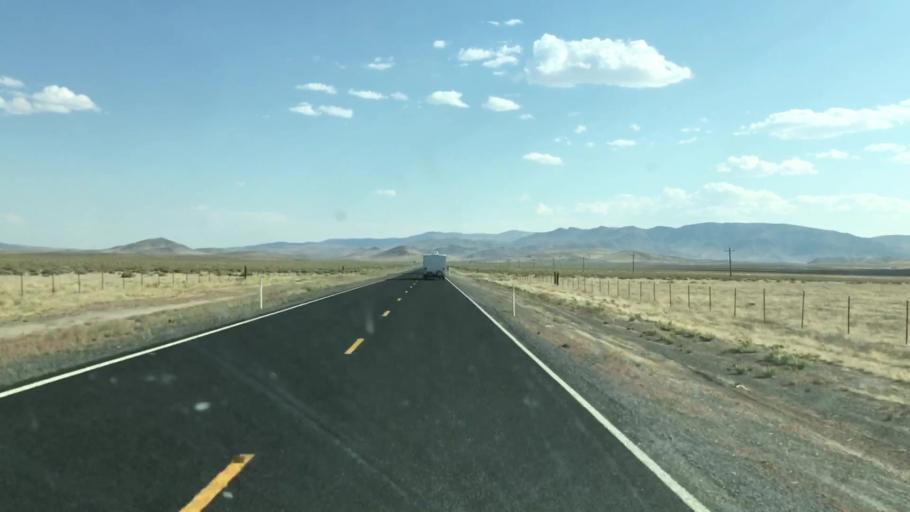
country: US
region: Nevada
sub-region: Lyon County
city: Fernley
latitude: 39.6768
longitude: -119.3334
